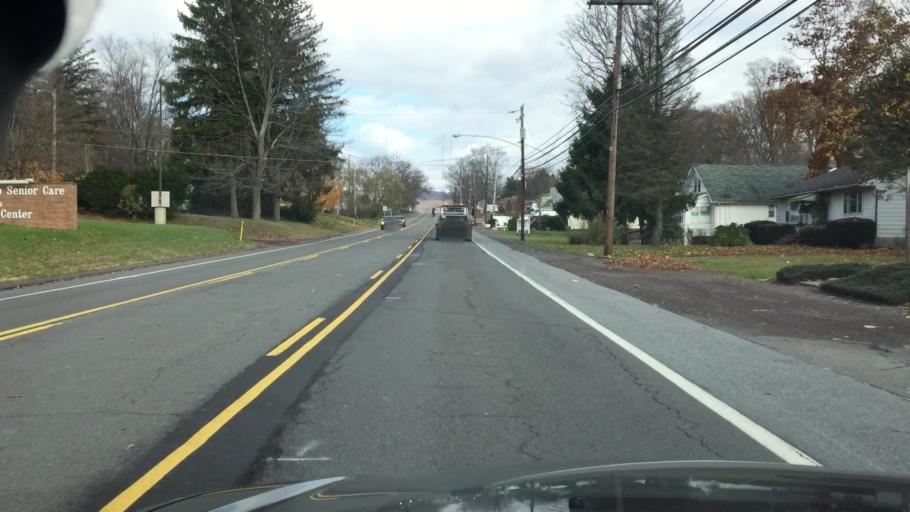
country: US
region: Pennsylvania
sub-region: Luzerne County
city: Mountain Top
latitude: 41.1514
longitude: -75.8946
